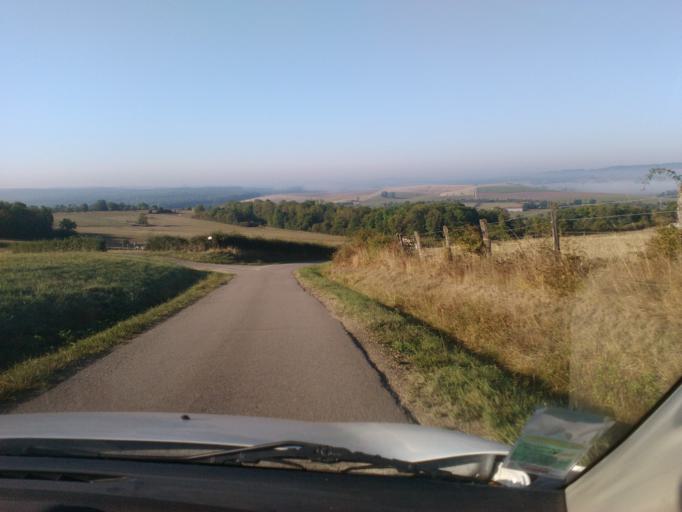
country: FR
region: Lorraine
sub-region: Departement des Vosges
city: Mirecourt
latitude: 48.2677
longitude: 6.1836
